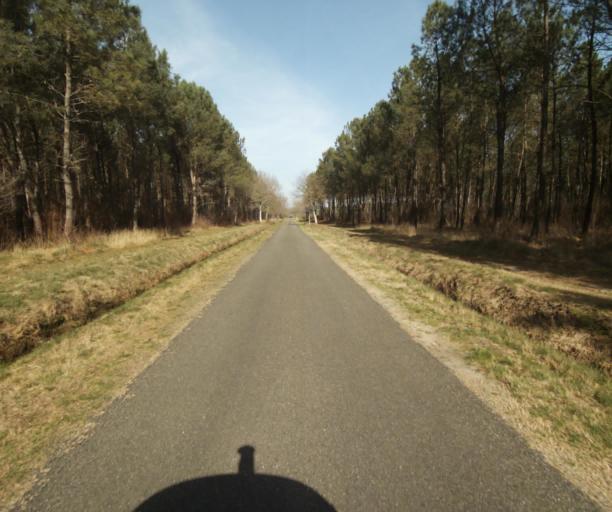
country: FR
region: Aquitaine
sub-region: Departement de la Gironde
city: Bazas
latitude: 44.2217
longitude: -0.2047
